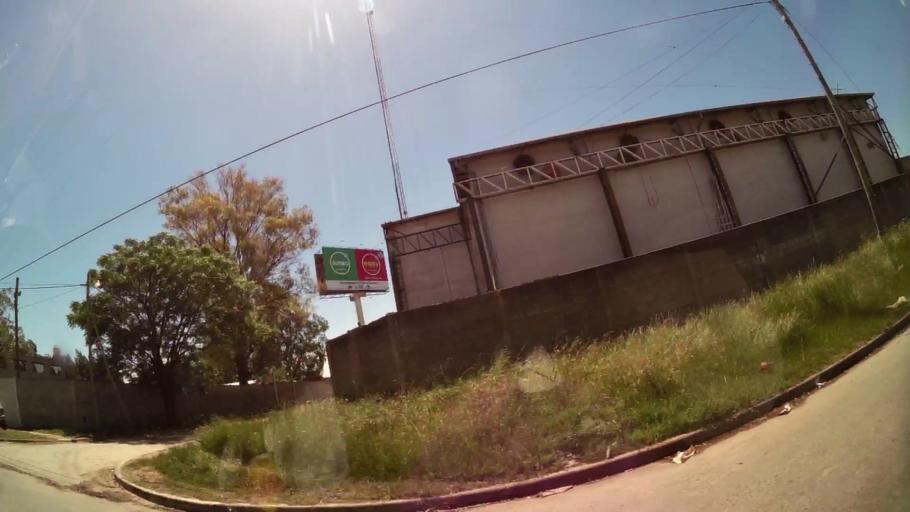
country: AR
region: Buenos Aires
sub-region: Partido de Tigre
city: Tigre
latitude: -34.4808
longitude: -58.6463
